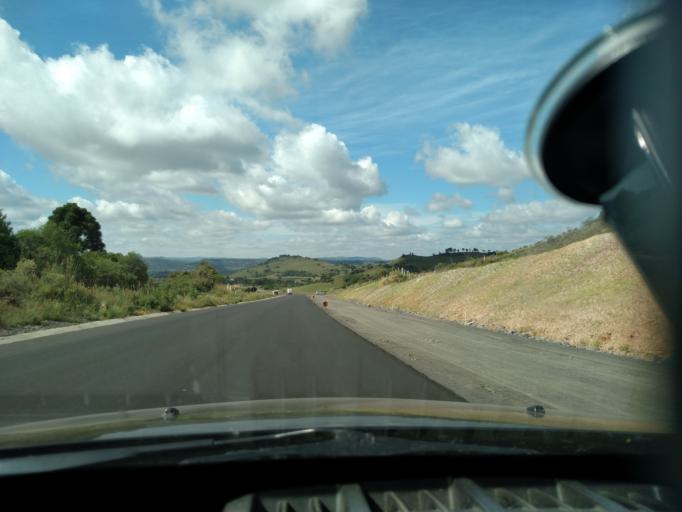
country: BR
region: Santa Catarina
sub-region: Sao Joaquim
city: Sao Joaquim
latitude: -28.0646
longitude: -50.0733
